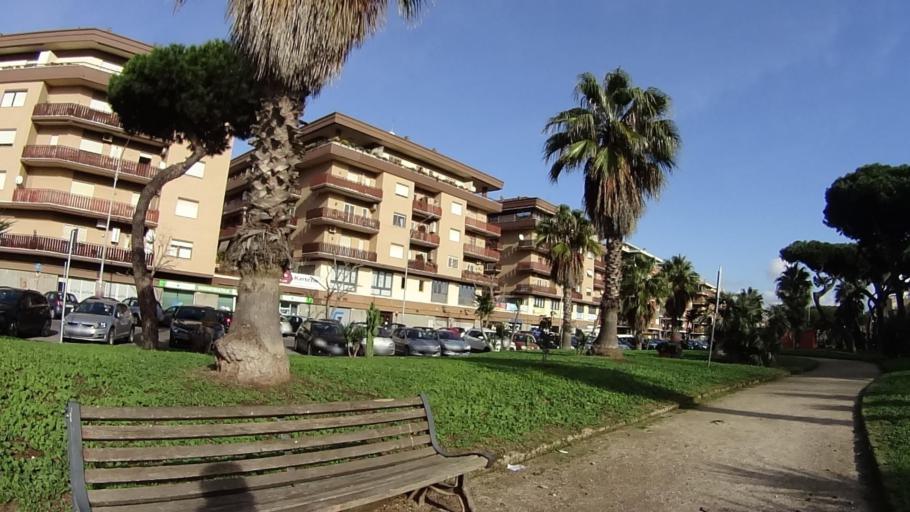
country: IT
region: Latium
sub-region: Citta metropolitana di Roma Capitale
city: Lido di Ostia
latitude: 41.7368
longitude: 12.2696
